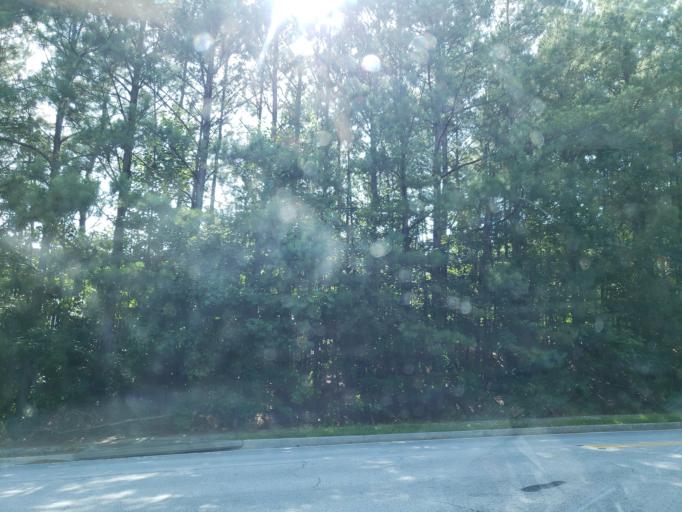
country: US
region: Georgia
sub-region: Cobb County
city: Mableton
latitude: 33.8559
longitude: -84.5671
